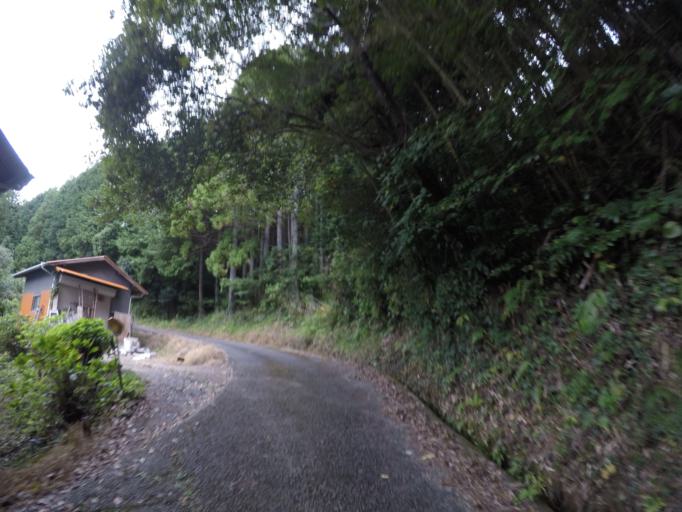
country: JP
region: Shizuoka
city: Shimada
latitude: 34.8883
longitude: 138.1661
